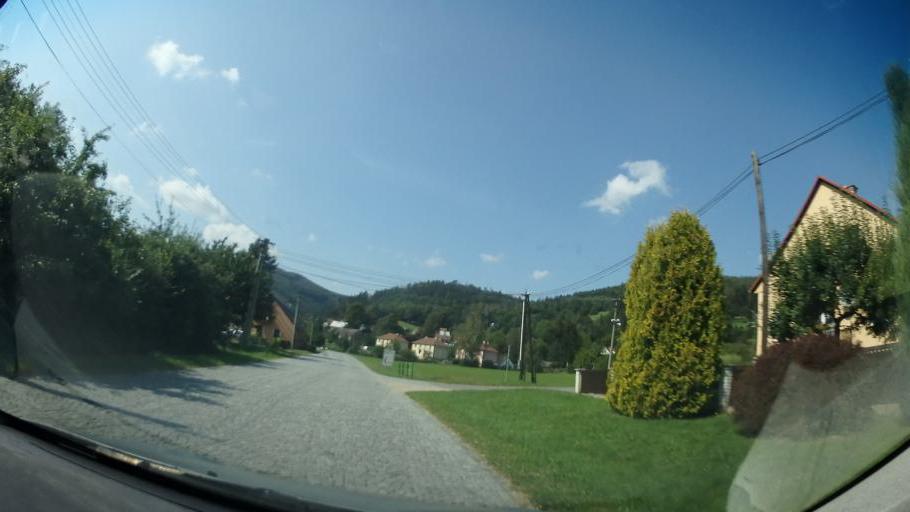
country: CZ
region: Vysocina
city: Bystrice nad Pernstejnem
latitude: 49.5571
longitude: 16.3258
